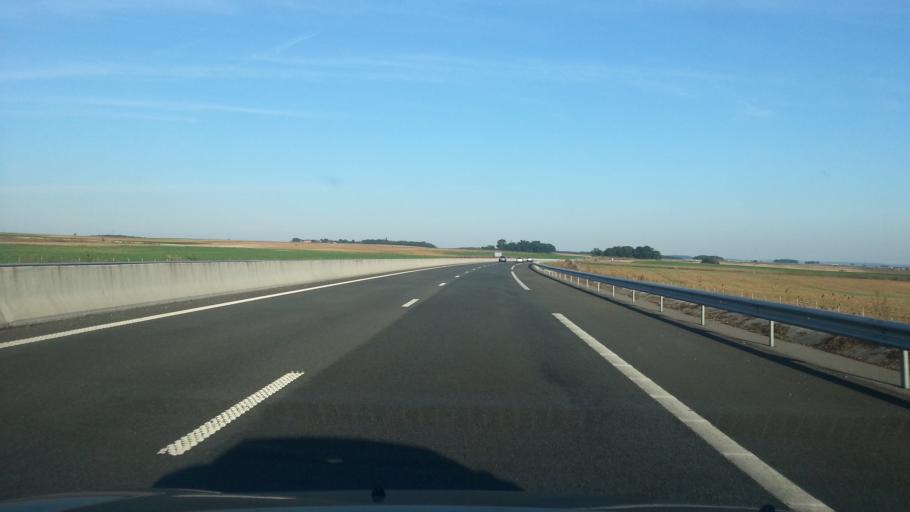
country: FR
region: Picardie
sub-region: Departement de l'Oise
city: Catenoy
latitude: 49.3848
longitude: 2.4875
